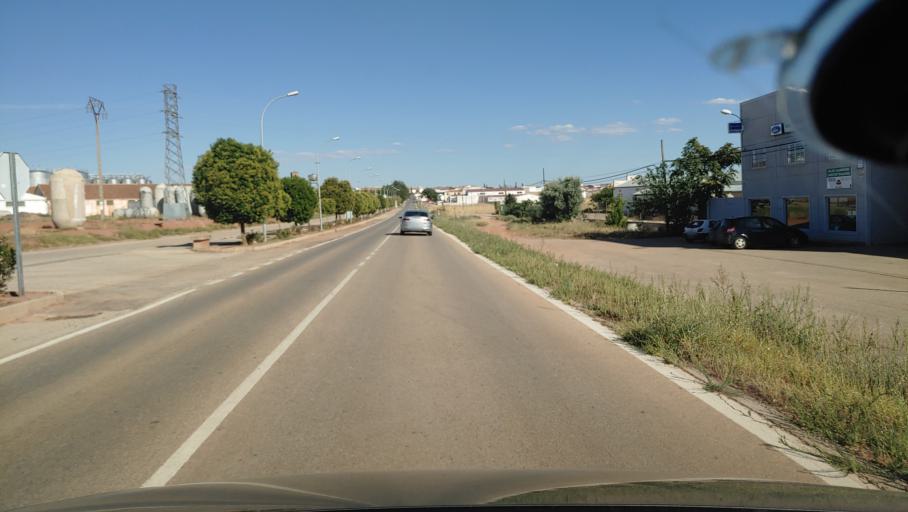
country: ES
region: Castille-La Mancha
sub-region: Provincia de Ciudad Real
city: Infantes
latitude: 38.7384
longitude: -3.0251
